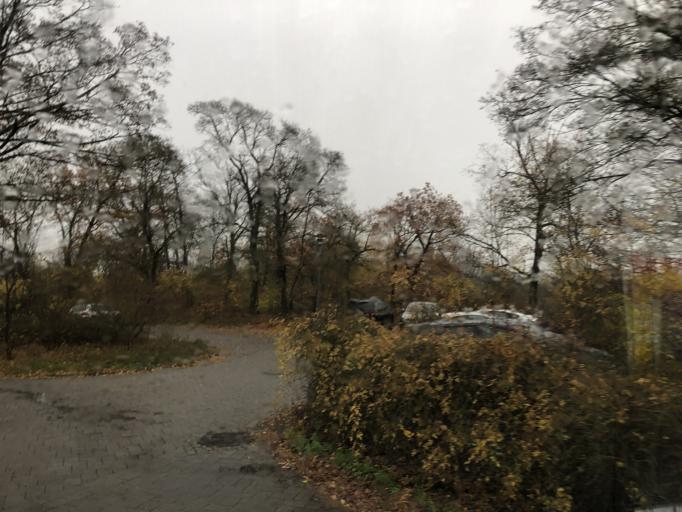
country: DE
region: Saxony-Anhalt
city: Halle Neustadt
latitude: 51.4931
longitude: 11.9402
